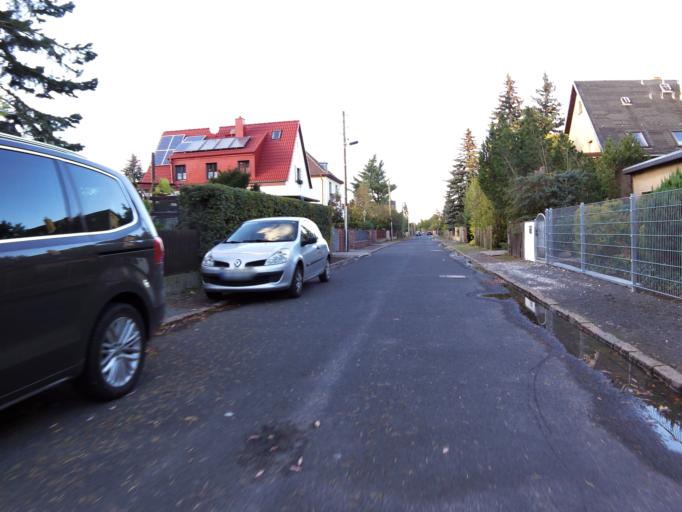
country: DE
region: Saxony
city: Grossposna
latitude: 51.3204
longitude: 12.4613
